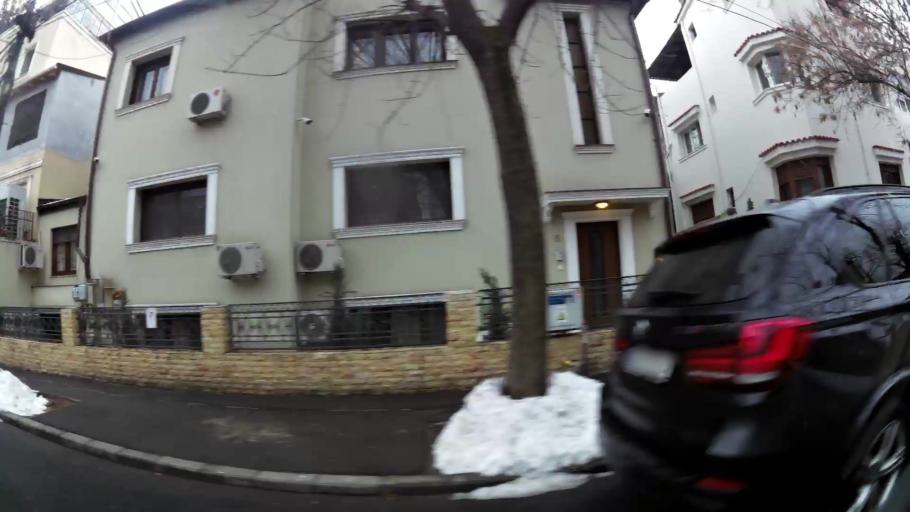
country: RO
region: Bucuresti
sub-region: Municipiul Bucuresti
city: Bucharest
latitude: 44.4629
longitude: 26.0942
